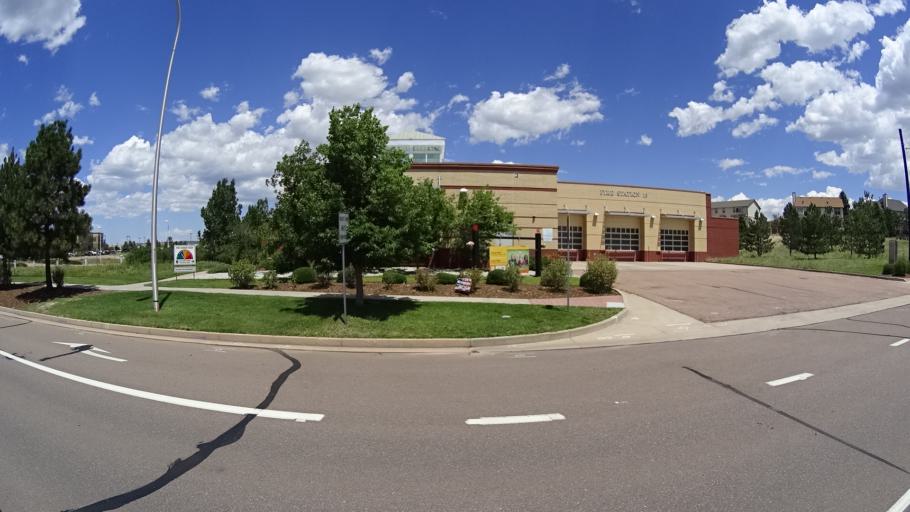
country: US
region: Colorado
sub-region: El Paso County
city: Air Force Academy
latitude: 38.9597
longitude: -104.7812
